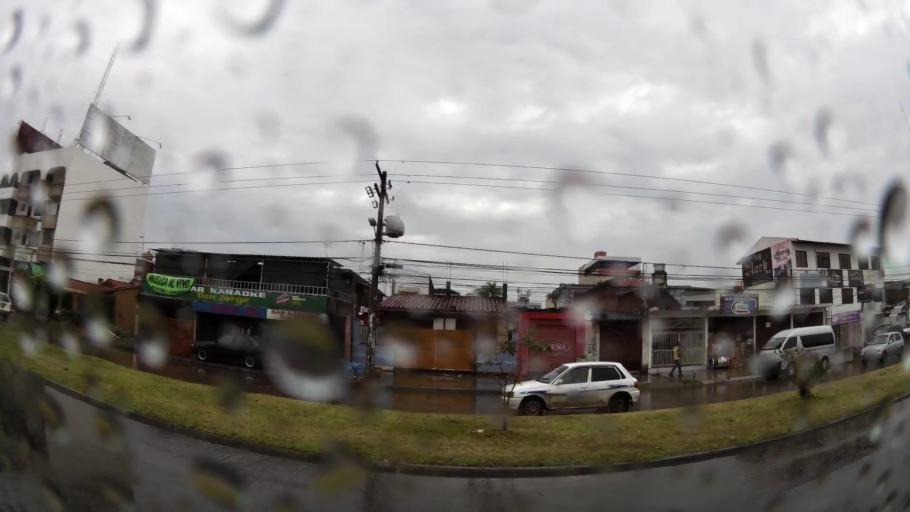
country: BO
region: Santa Cruz
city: Santa Cruz de la Sierra
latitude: -17.7892
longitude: -63.1649
